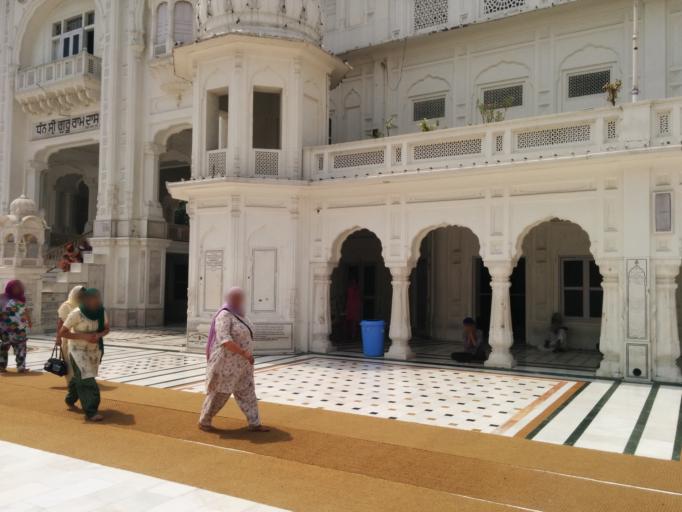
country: IN
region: Punjab
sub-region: Amritsar
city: Amritsar
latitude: 31.6195
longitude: 74.8759
